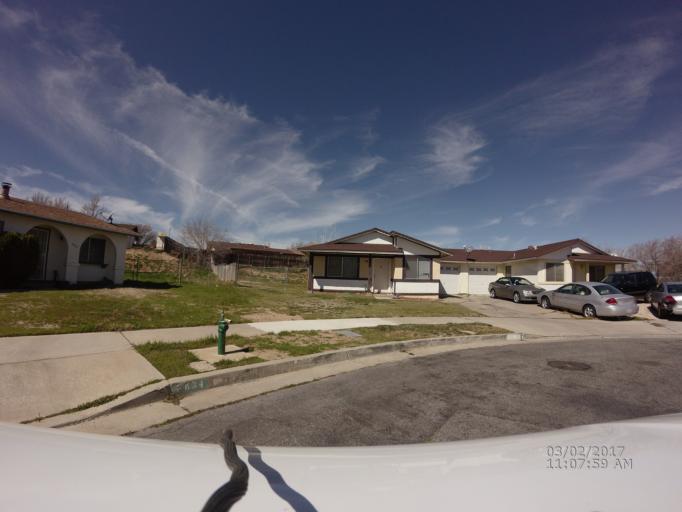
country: US
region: California
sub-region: Los Angeles County
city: Quartz Hill
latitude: 34.6466
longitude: -118.2524
